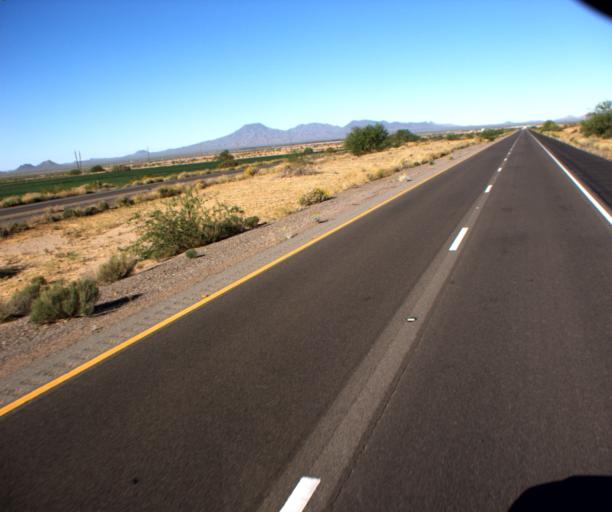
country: US
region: Arizona
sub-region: Pinal County
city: Casa Grande
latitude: 32.8284
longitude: -111.9256
